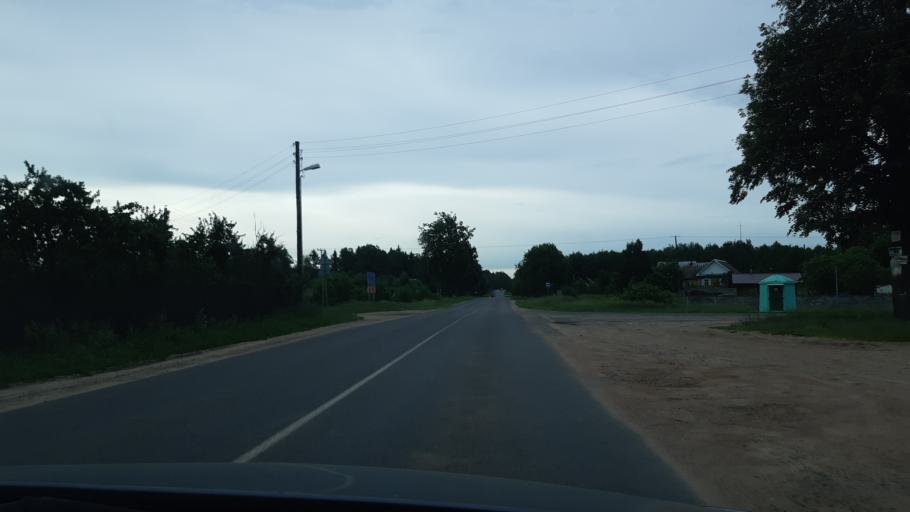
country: BY
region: Minsk
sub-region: Smalyavitski Rayon
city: Oktjabr'skij
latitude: 54.1113
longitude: 28.1843
